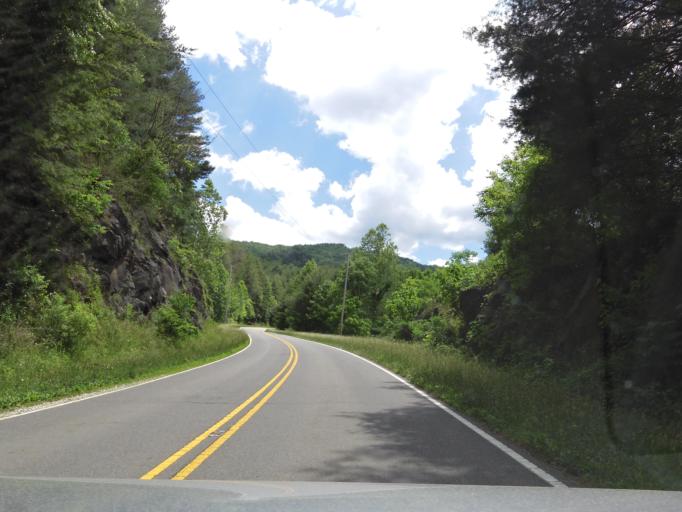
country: US
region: North Carolina
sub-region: Graham County
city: Robbinsville
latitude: 35.3853
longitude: -83.8630
